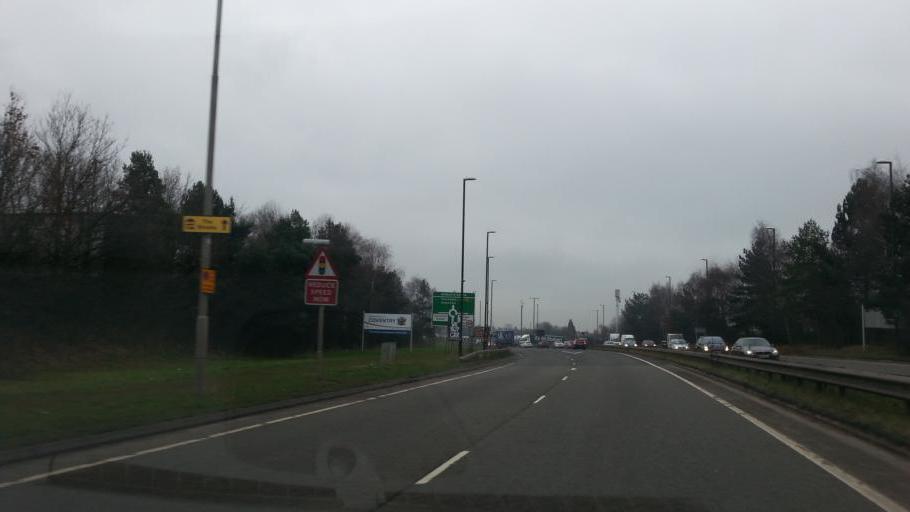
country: GB
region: England
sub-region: Warwickshire
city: Exhall
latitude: 52.4514
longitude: -1.5000
